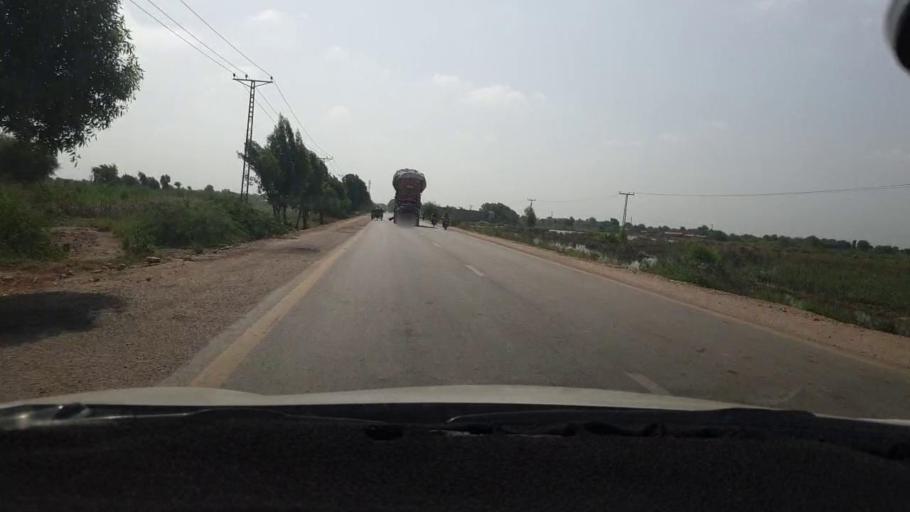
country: PK
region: Sindh
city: Mirpur Khas
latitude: 25.7173
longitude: 69.1211
